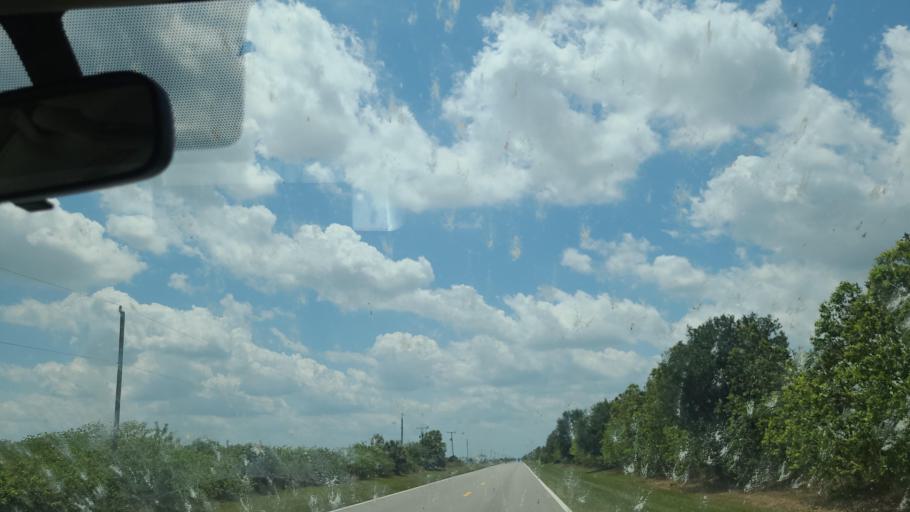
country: US
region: Florida
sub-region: Glades County
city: Buckhead Ridge
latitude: 27.2792
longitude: -81.0542
